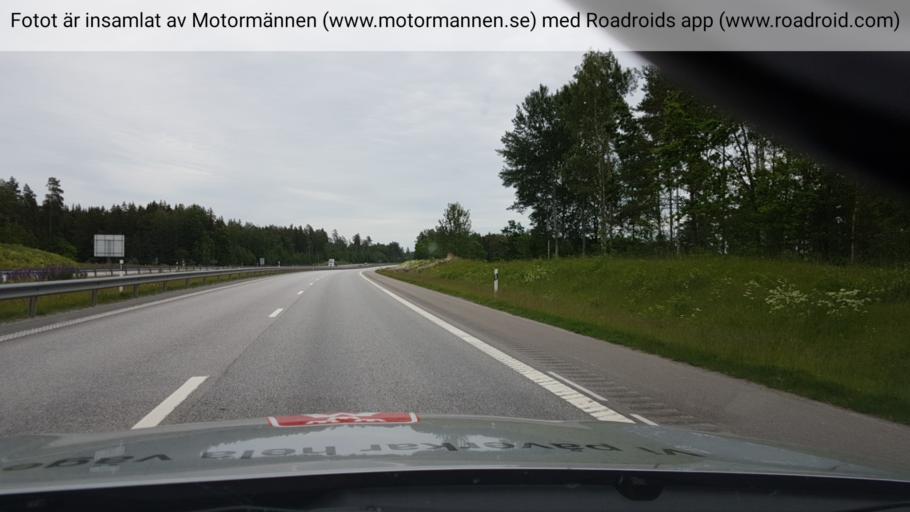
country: SE
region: OErebro
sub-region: Lindesbergs Kommun
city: Frovi
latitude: 59.3145
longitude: 15.4372
